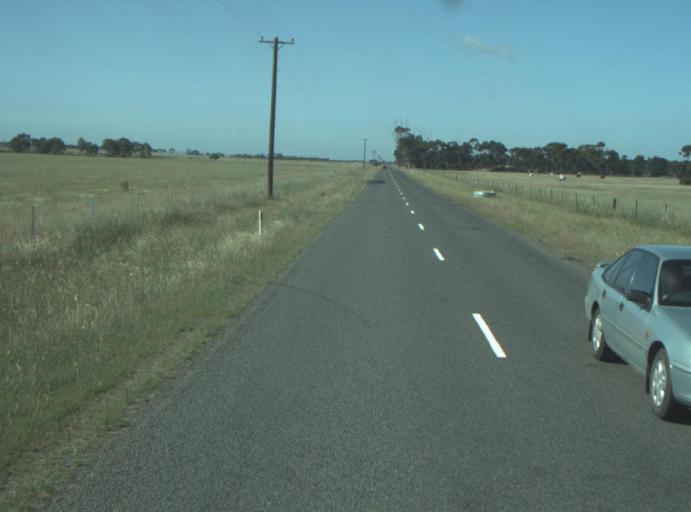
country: AU
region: Victoria
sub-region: Wyndham
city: Little River
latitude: -37.9665
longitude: 144.4624
